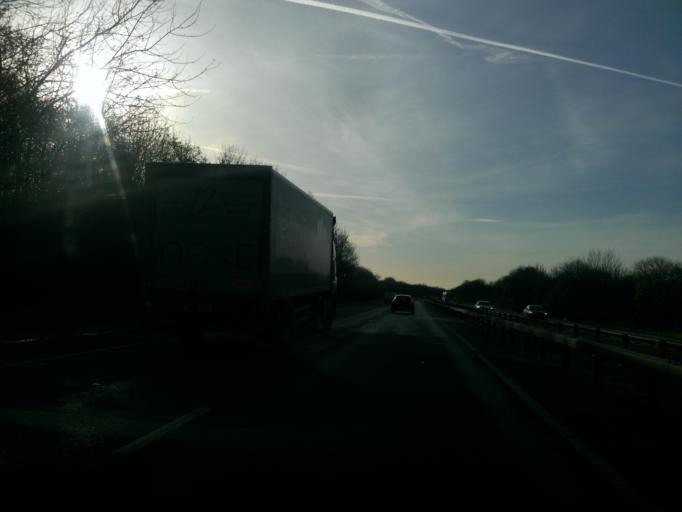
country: GB
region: England
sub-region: Essex
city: Witham
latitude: 51.7986
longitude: 0.6519
